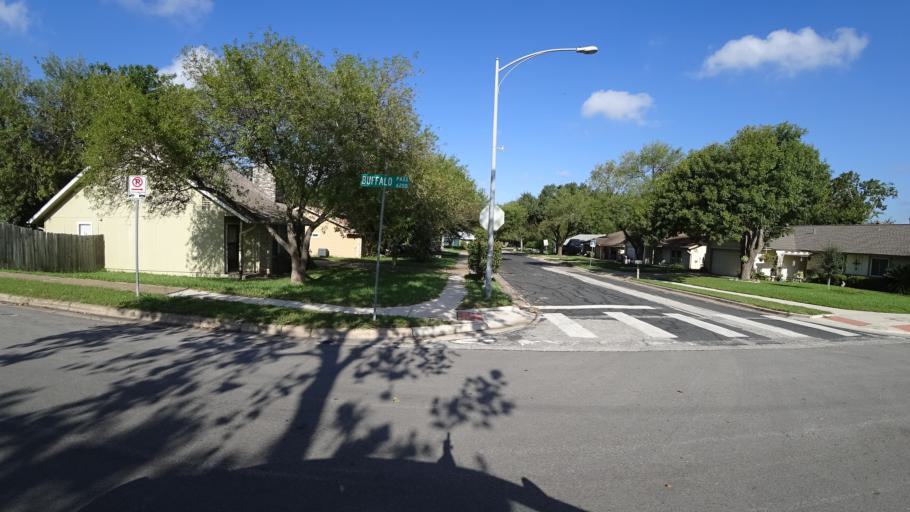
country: US
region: Texas
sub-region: Travis County
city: Rollingwood
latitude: 30.2105
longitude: -97.8069
